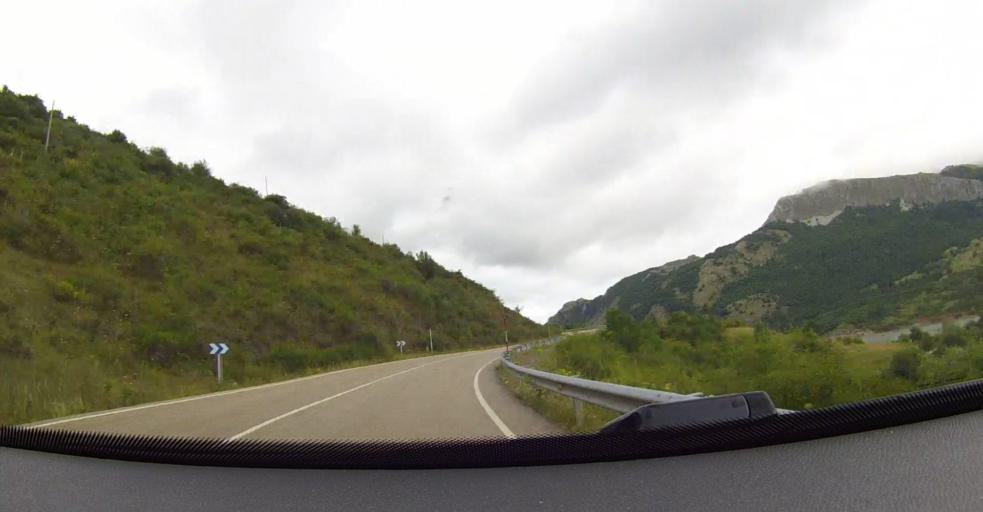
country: ES
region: Castille and Leon
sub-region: Provincia de Leon
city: Buron
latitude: 43.0234
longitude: -5.0443
